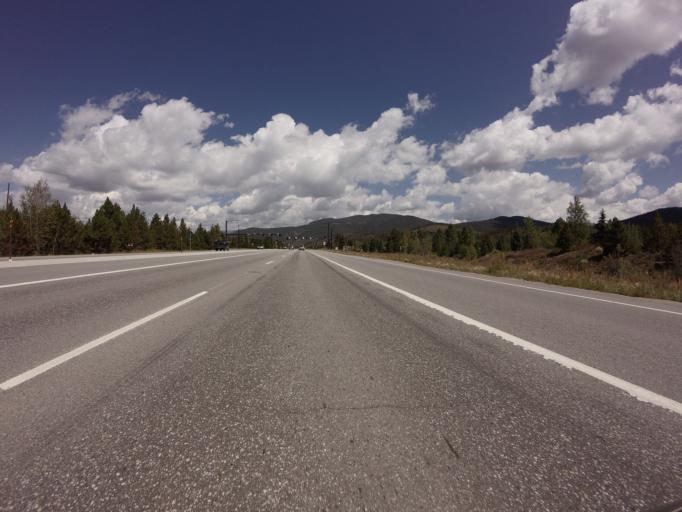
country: US
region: Colorado
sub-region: Summit County
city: Breckenridge
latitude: 39.5312
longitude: -106.0441
